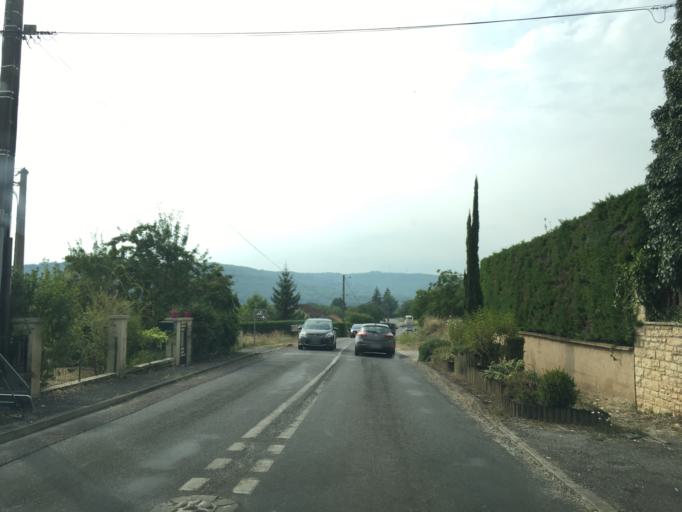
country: FR
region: Midi-Pyrenees
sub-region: Departement du Lot
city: Souillac
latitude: 44.8569
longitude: 1.5078
